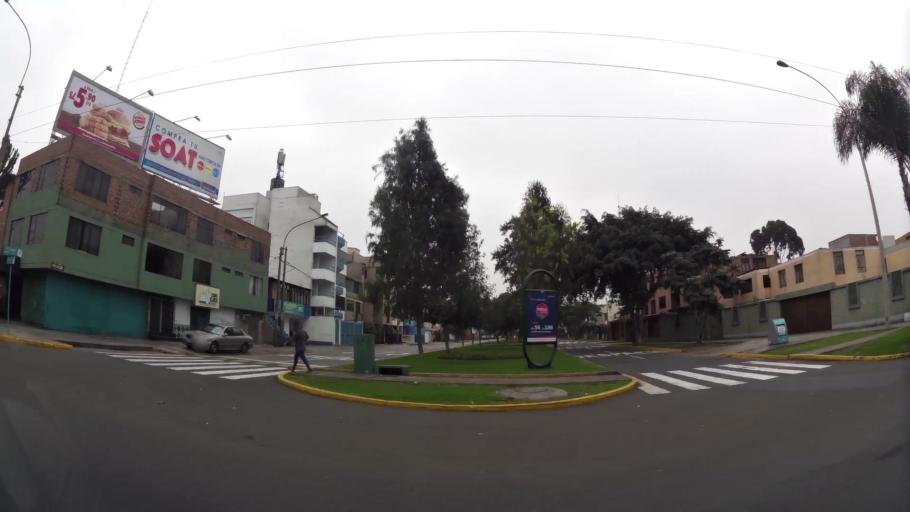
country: PE
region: Lima
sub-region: Lima
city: San Luis
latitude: -12.1070
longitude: -77.0008
